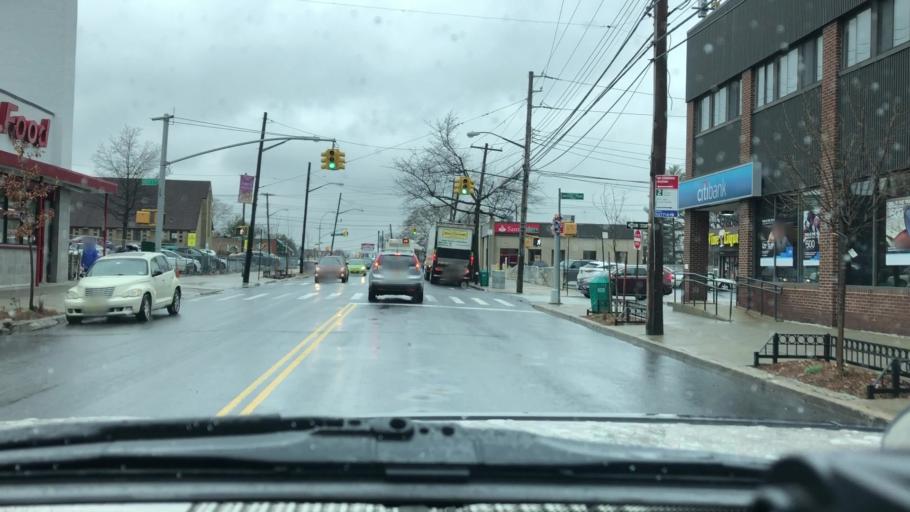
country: US
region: New Jersey
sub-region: Hudson County
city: Bayonne
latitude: 40.6307
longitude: -74.1043
